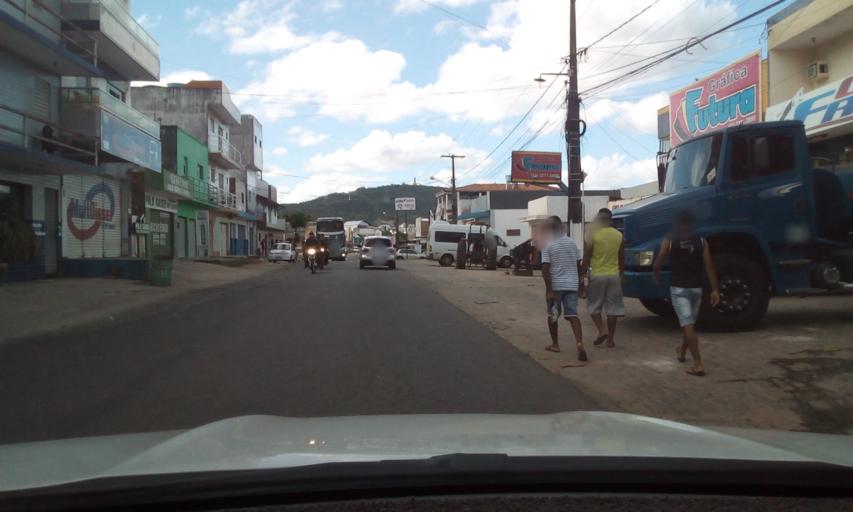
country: BR
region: Paraiba
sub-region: Guarabira
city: Guarabira
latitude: -6.8567
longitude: -35.4963
